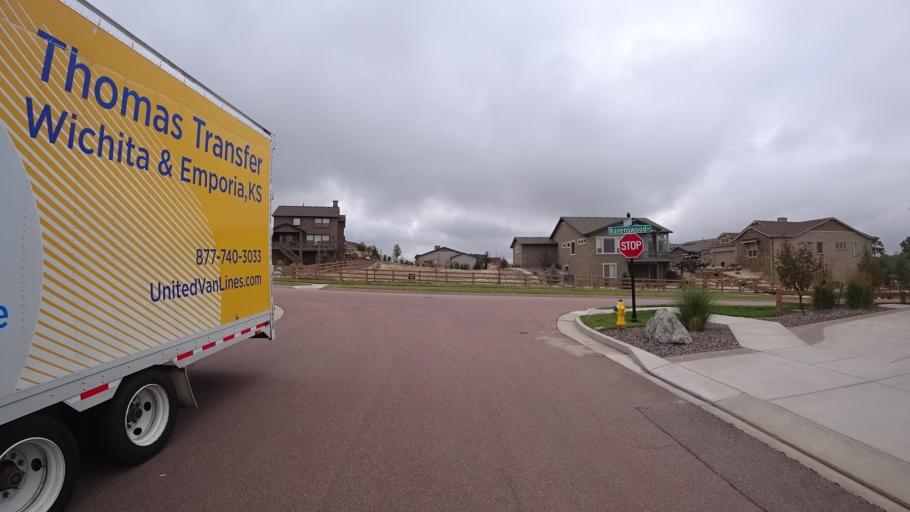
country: US
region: Colorado
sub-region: El Paso County
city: Gleneagle
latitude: 39.0116
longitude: -104.7879
